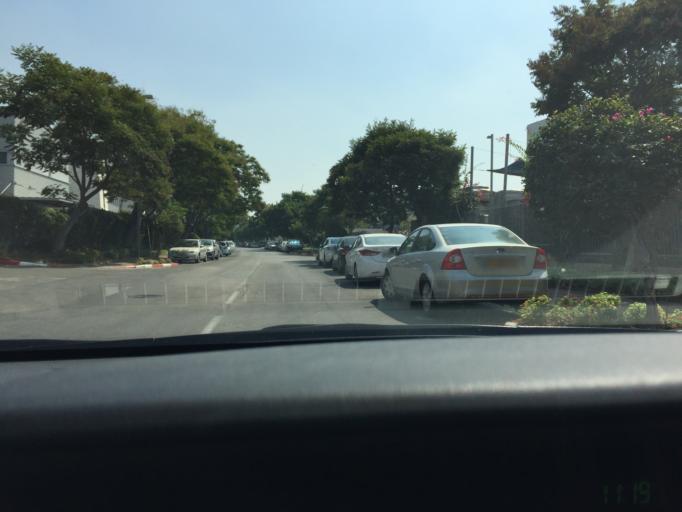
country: IL
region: Central District
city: Yehud
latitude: 31.9906
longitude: 34.9104
